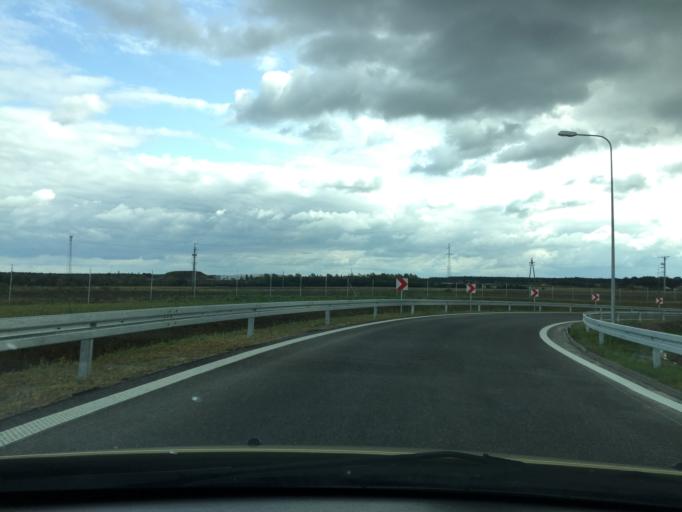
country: PL
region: Greater Poland Voivodeship
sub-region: Powiat jarocinski
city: Jarocin
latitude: 51.9791
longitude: 17.5256
